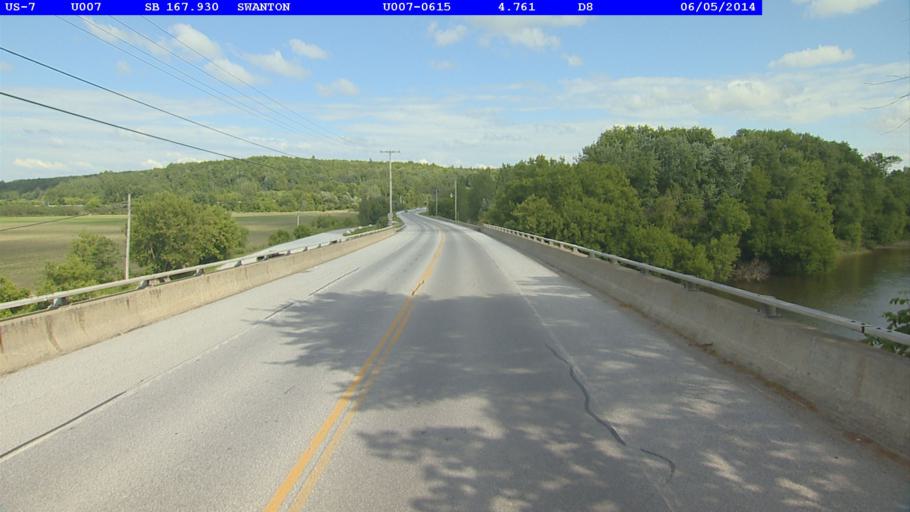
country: US
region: Vermont
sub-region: Franklin County
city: Swanton
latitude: 44.9103
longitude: -73.1071
